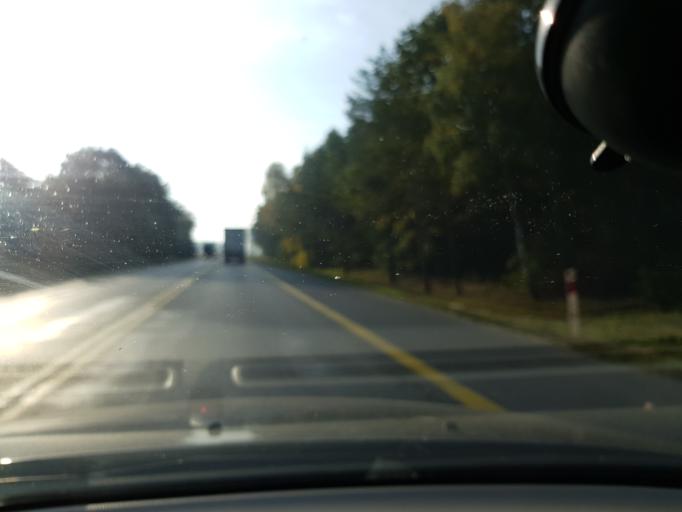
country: PL
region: Masovian Voivodeship
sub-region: Powiat otwocki
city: Otwock
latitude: 52.1479
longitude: 21.3208
